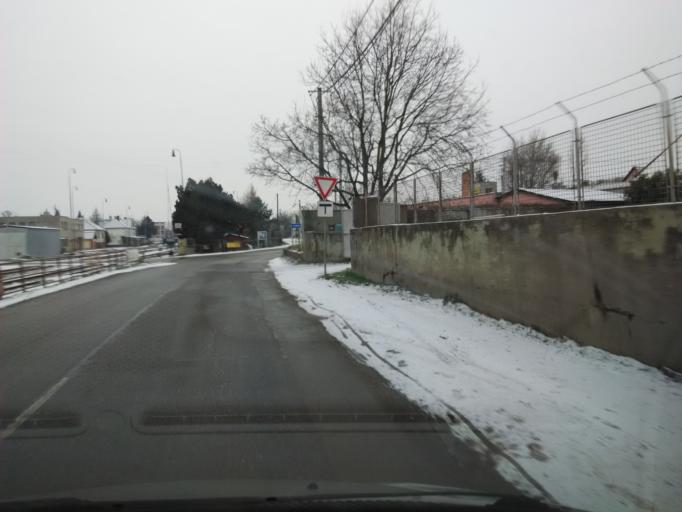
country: SK
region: Nitriansky
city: Zlate Moravce
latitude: 48.3881
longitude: 18.3775
